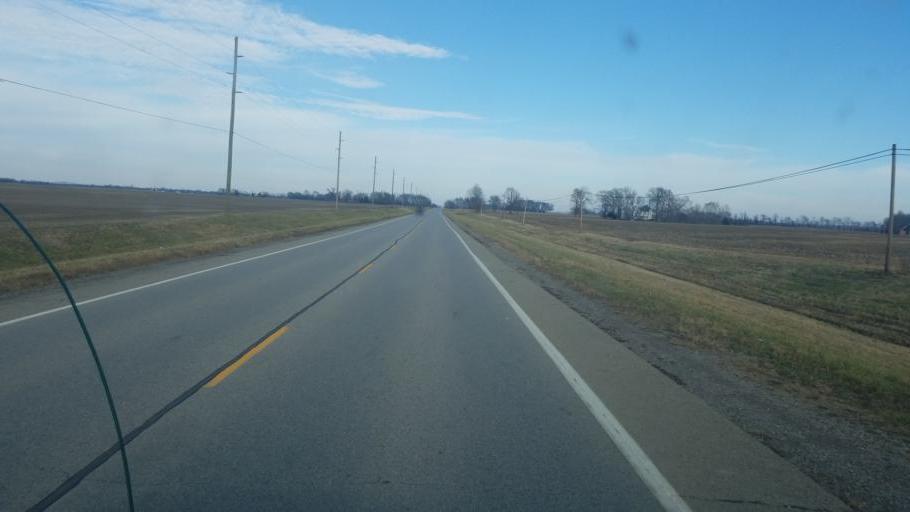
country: US
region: Illinois
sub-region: White County
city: Carmi
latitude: 38.1108
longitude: -88.1213
